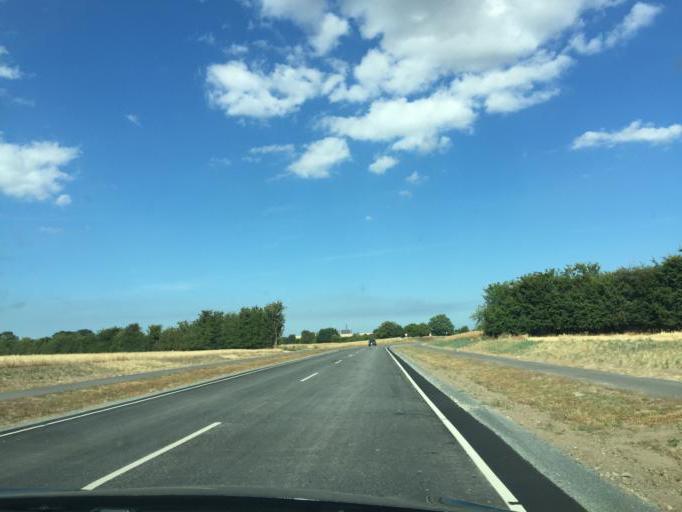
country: DK
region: South Denmark
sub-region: Odense Kommune
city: Hojby
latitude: 55.3433
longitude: 10.3911
